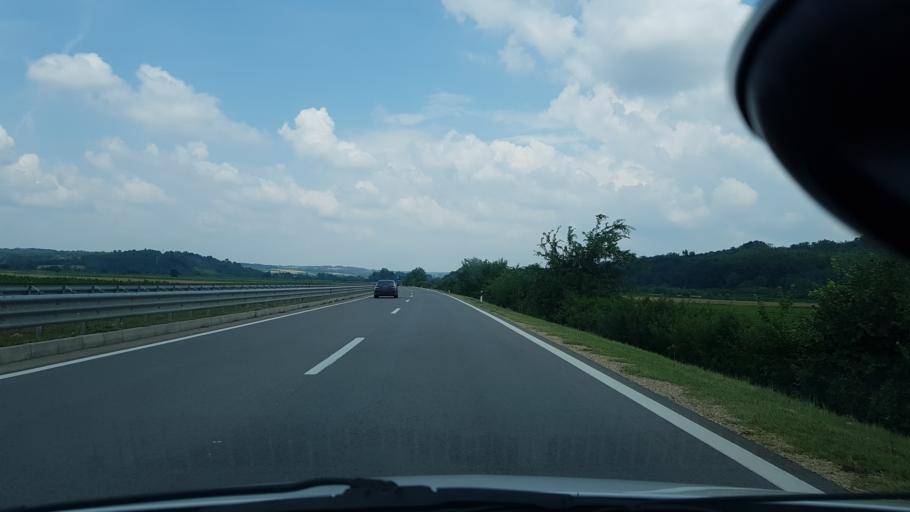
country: RS
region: Central Serbia
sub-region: Sumadijski Okrug
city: Batocina
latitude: 44.1279
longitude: 21.0185
